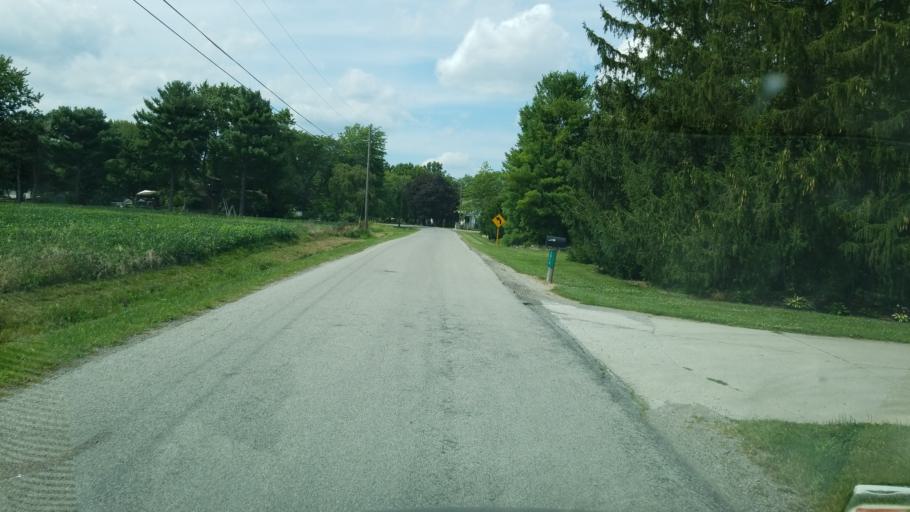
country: US
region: Ohio
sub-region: Marion County
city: Marion
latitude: 40.5297
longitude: -83.0926
